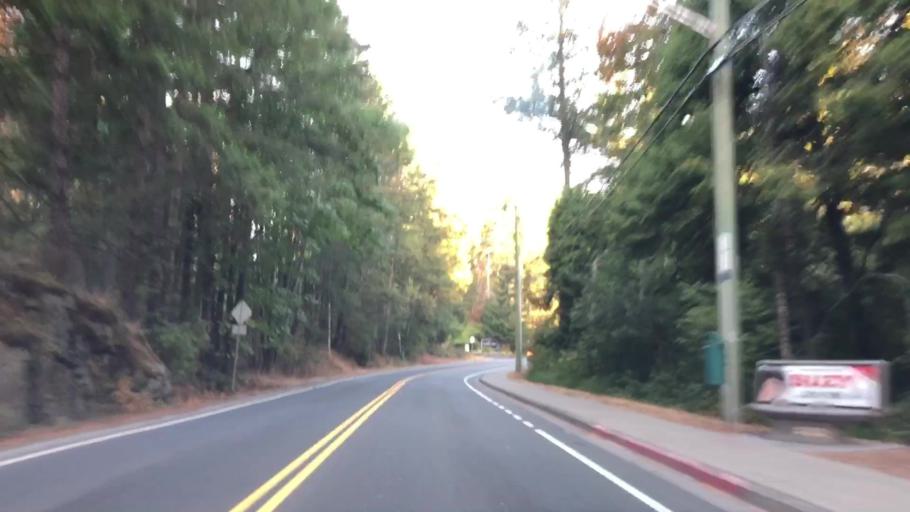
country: CA
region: British Columbia
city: Colwood
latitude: 48.4090
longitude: -123.5104
